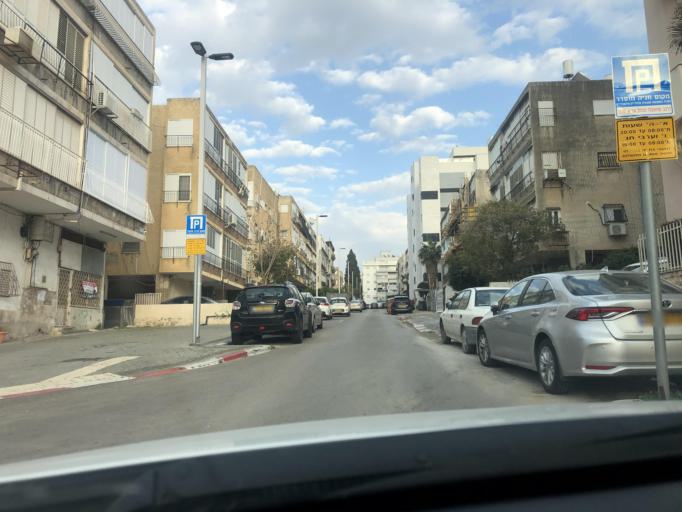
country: IL
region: Tel Aviv
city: Bat Yam
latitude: 32.0227
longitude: 34.7523
